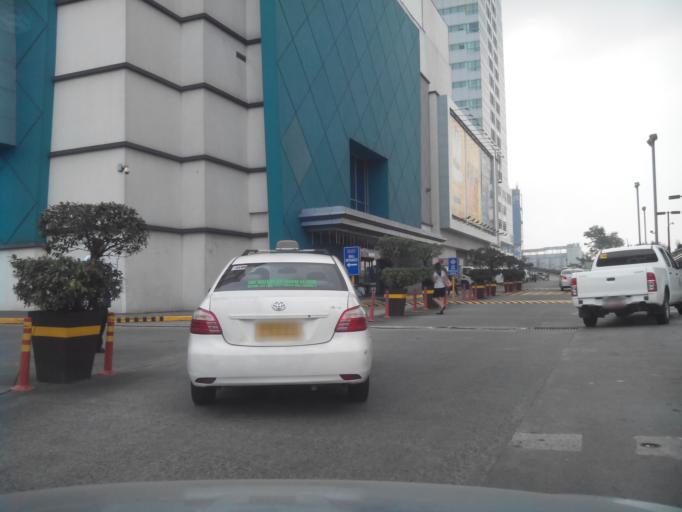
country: PH
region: Metro Manila
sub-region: Mandaluyong
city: Mandaluyong City
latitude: 14.5706
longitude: 121.0469
